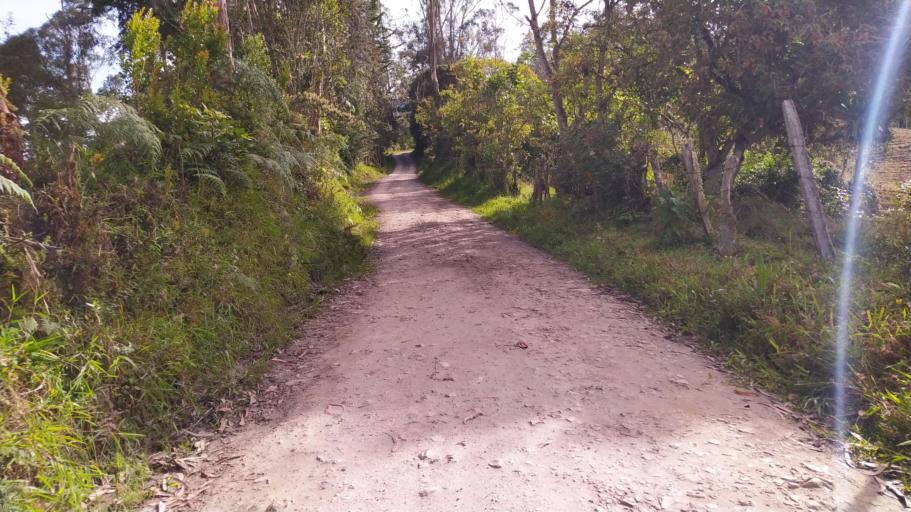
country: CO
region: Cundinamarca
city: Tenza
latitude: 5.0896
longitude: -73.4680
